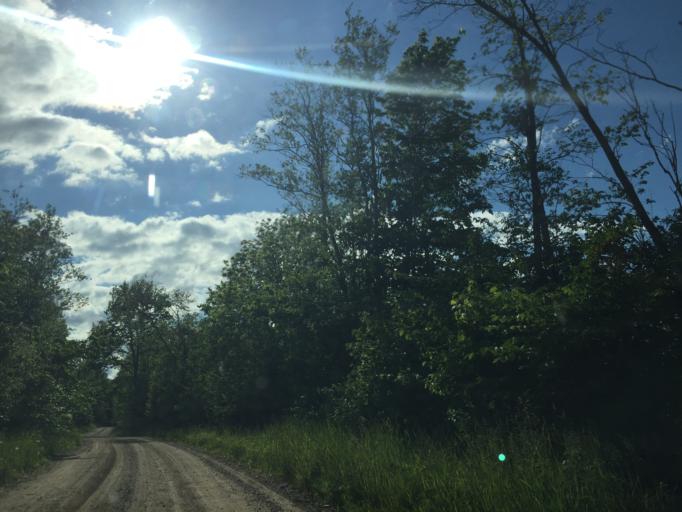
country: LV
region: Talsu Rajons
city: Sabile
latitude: 57.0123
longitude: 22.6408
